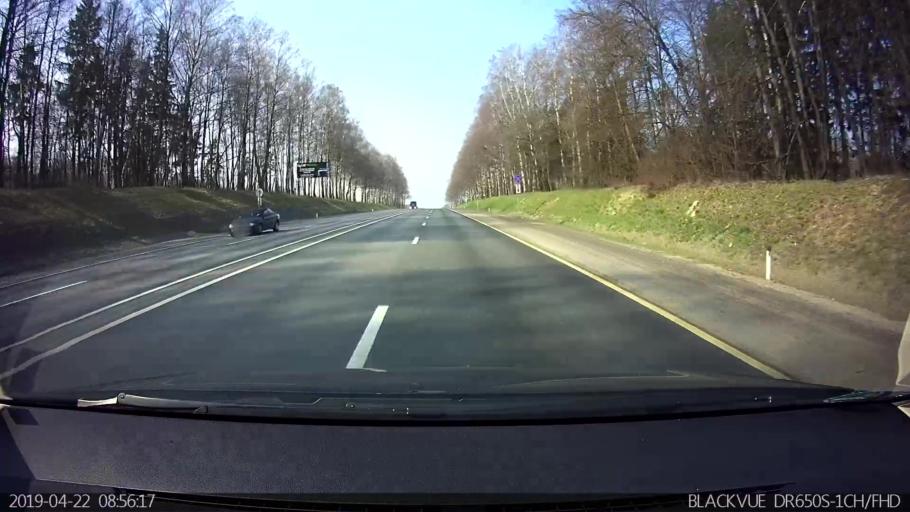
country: RU
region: Smolensk
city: Pechersk
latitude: 54.8757
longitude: 32.0428
